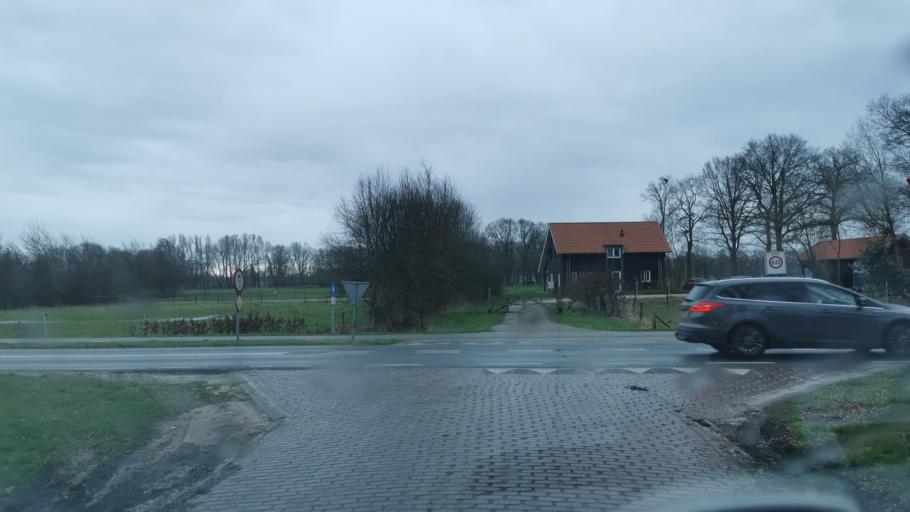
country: NL
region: Overijssel
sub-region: Gemeente Losser
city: Losser
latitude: 52.2619
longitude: 6.9793
